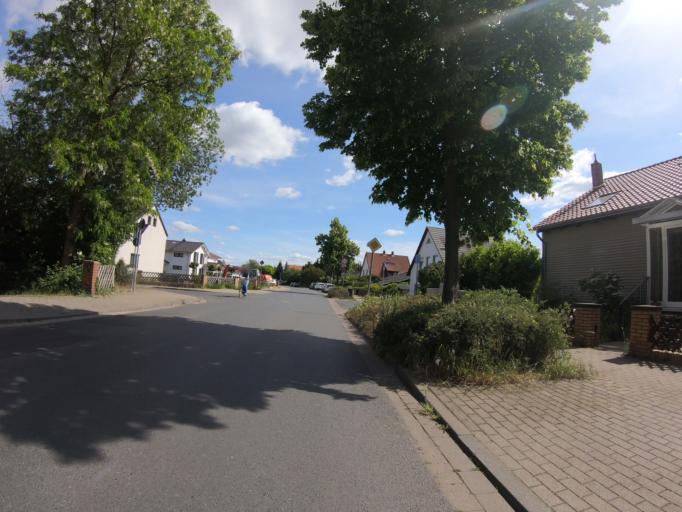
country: DE
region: Lower Saxony
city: Wolfenbuettel
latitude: 52.1789
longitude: 10.5320
